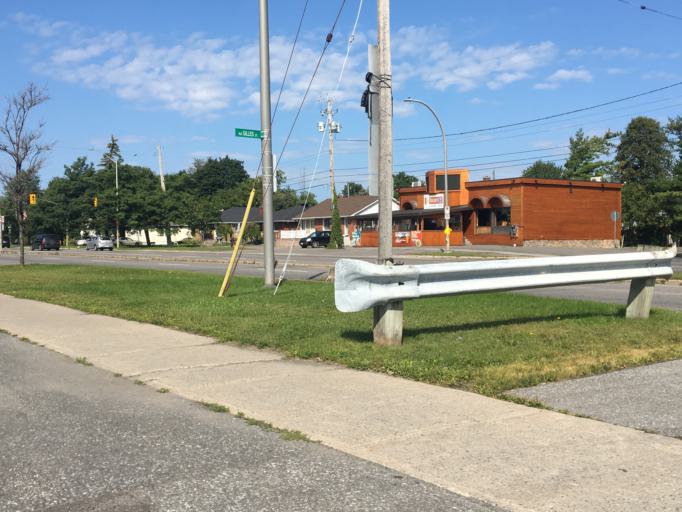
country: CA
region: Ontario
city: Ottawa
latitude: 45.3782
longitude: -75.6703
